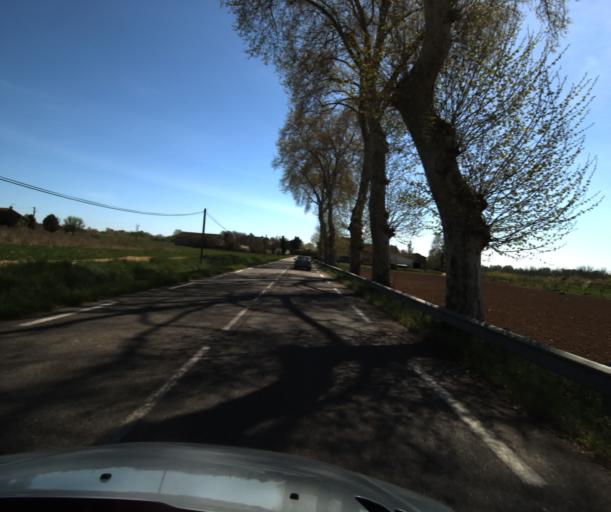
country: FR
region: Midi-Pyrenees
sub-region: Departement du Tarn-et-Garonne
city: Montbeton
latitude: 44.0731
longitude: 1.2846
